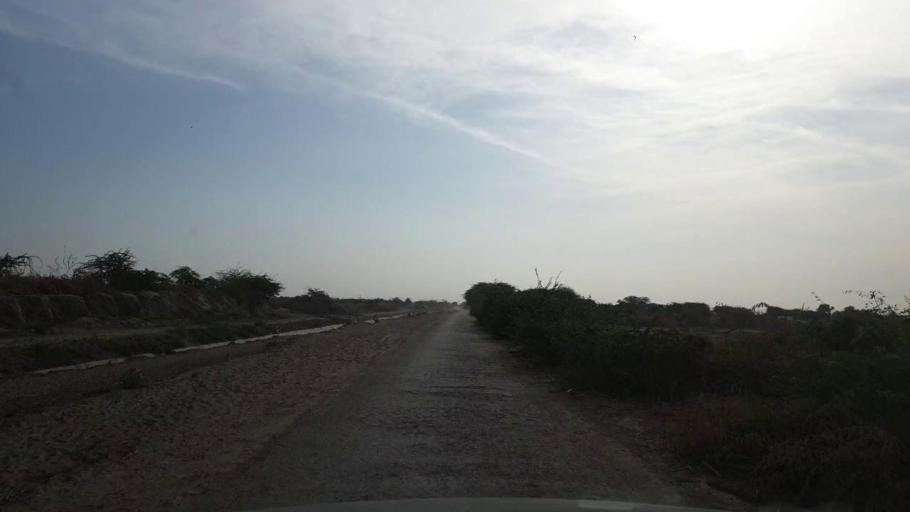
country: PK
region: Sindh
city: Kunri
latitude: 25.1529
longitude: 69.5092
